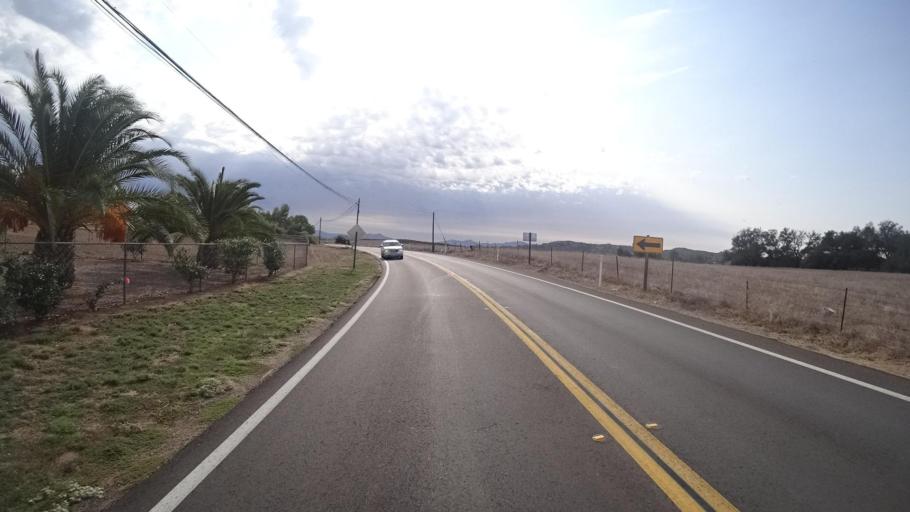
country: US
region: California
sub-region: San Diego County
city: Ramona
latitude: 33.0182
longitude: -116.9213
